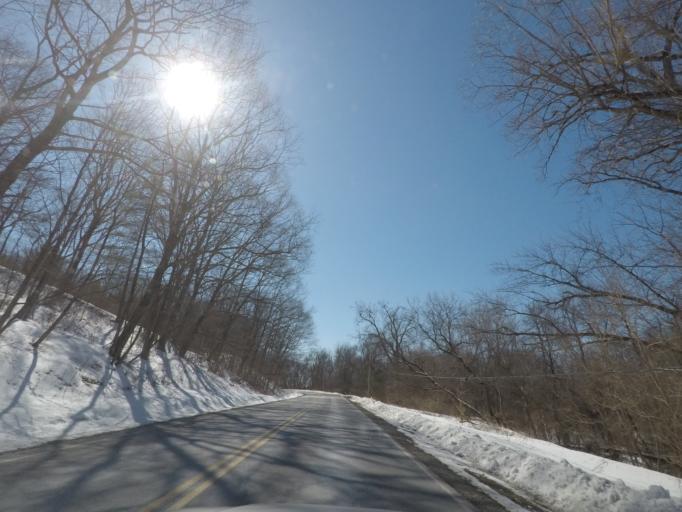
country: US
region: New York
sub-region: Saratoga County
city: Schuylerville
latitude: 43.0872
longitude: -73.5733
